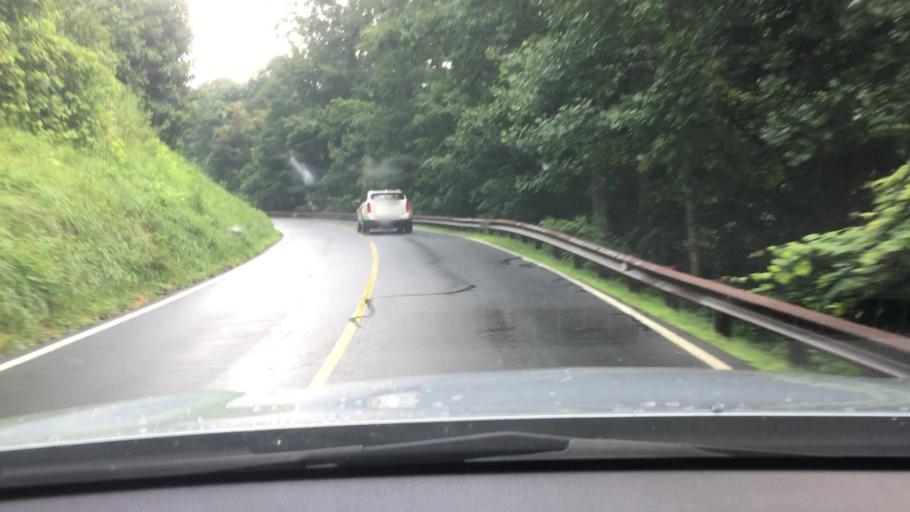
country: US
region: North Carolina
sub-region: Yancey County
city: Burnsville
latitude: 35.8854
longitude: -82.3521
